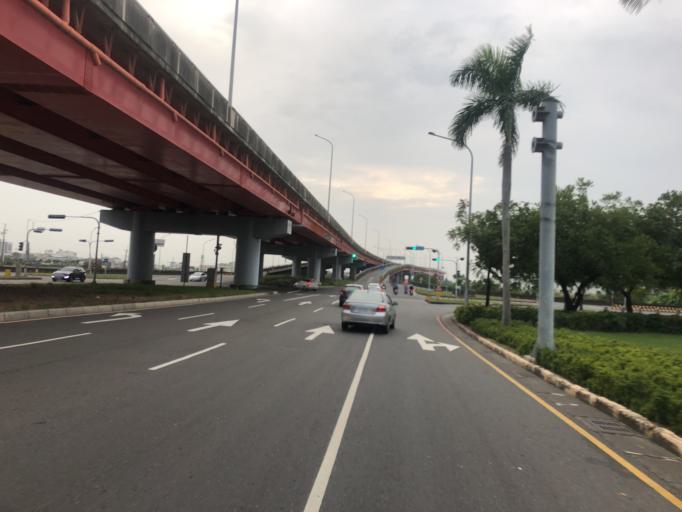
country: TW
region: Taiwan
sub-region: Tainan
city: Tainan
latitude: 23.0850
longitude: 120.2809
